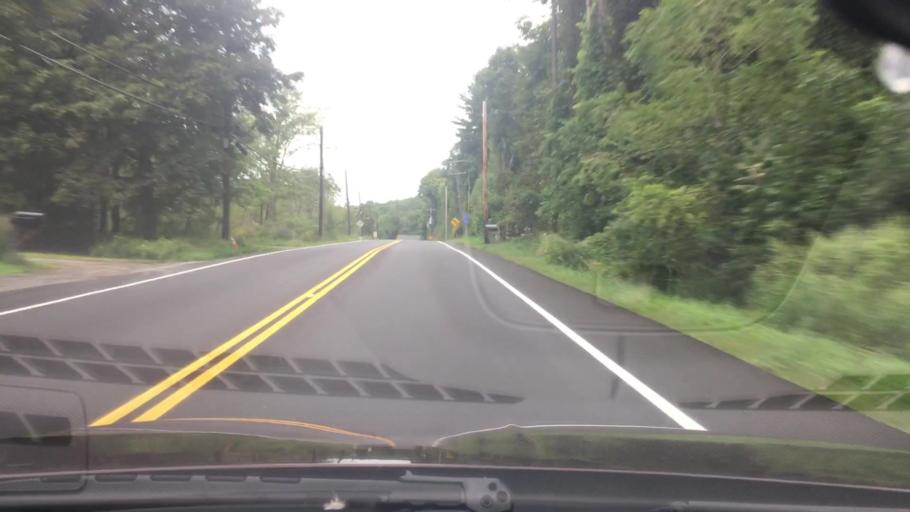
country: US
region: New York
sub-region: Dutchess County
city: Dover Plains
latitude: 41.8435
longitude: -73.5772
